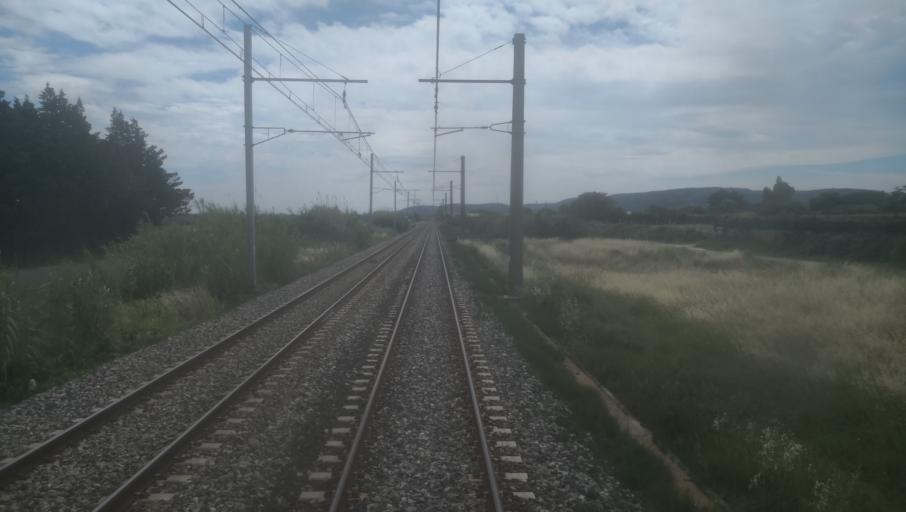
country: FR
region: Languedoc-Roussillon
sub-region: Departement de l'Herault
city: Mireval
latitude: 43.5139
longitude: 3.8172
